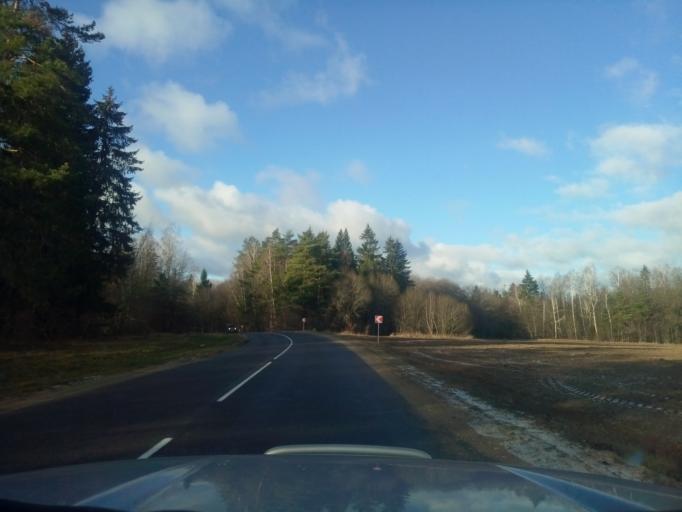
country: BY
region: Minsk
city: Kapyl'
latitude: 53.1745
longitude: 27.0180
